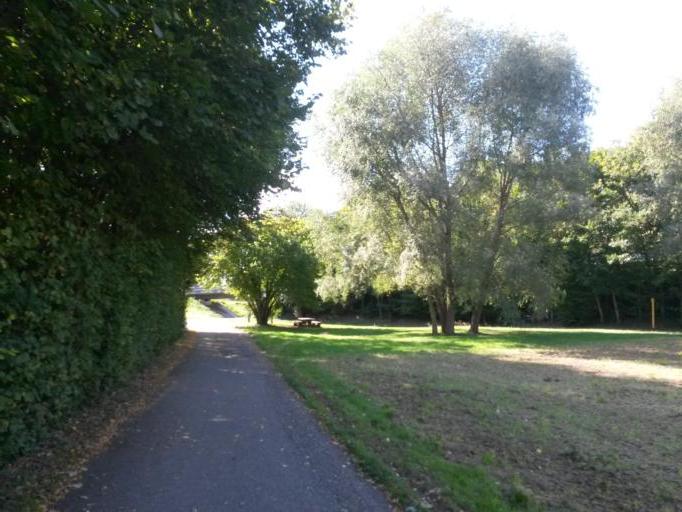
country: DE
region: Baden-Wuerttemberg
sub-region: Karlsruhe Region
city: Muhlacker
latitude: 48.9420
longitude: 8.8122
